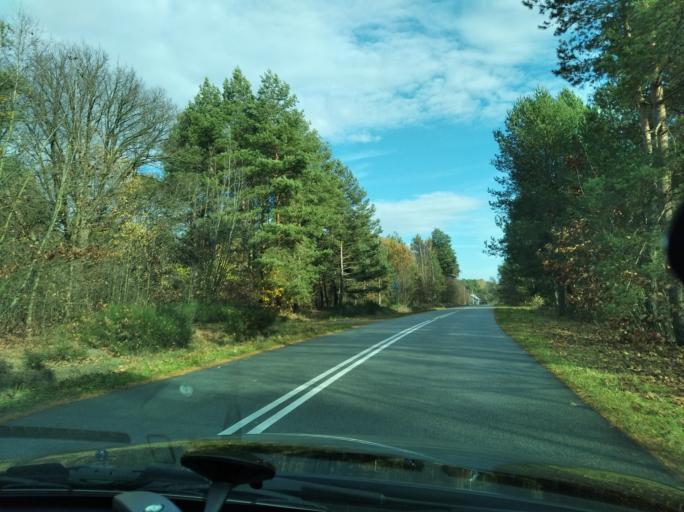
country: PL
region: Subcarpathian Voivodeship
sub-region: Powiat ropczycko-sedziszowski
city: Sedziszow Malopolski
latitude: 50.1131
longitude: 21.6869
